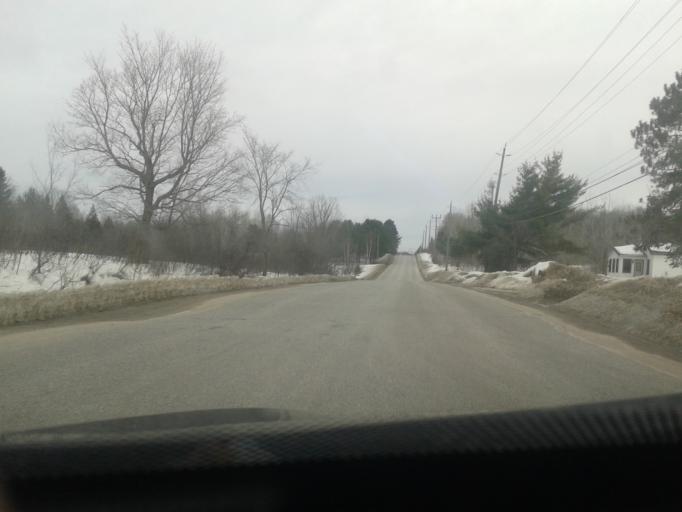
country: CA
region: Ontario
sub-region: Nipissing District
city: North Bay
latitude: 46.3471
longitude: -79.4812
